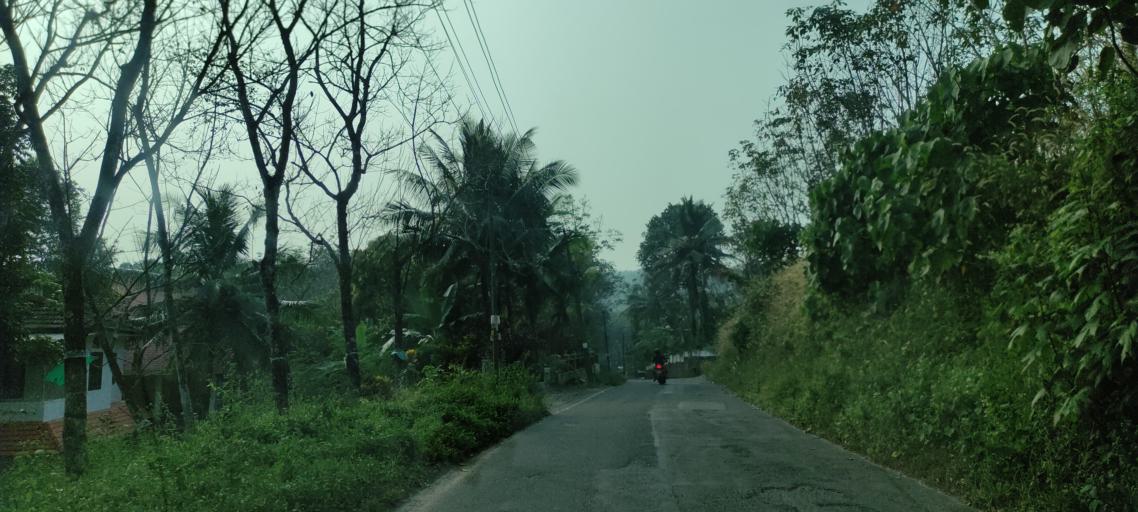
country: IN
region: Kerala
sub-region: Ernakulam
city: Piravam
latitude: 9.8000
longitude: 76.5014
